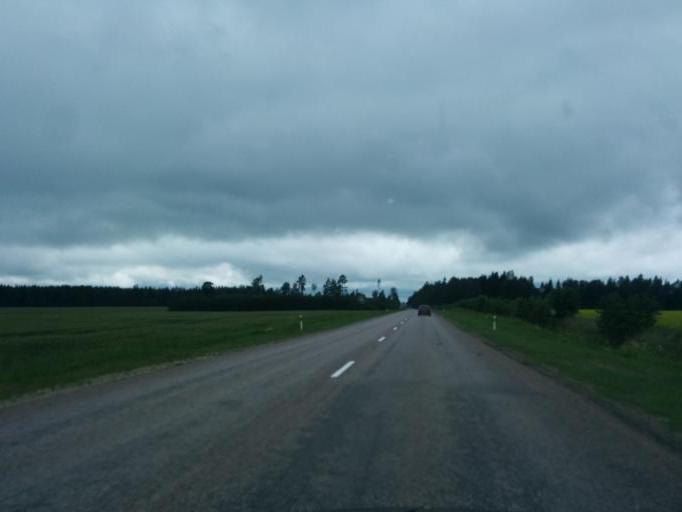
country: LV
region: Beverina
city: Murmuiza
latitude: 57.4860
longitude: 25.5951
